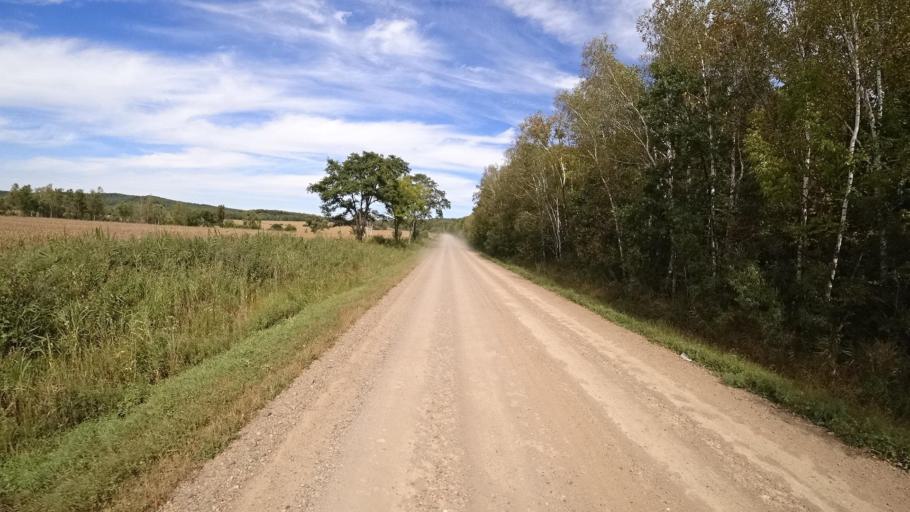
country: RU
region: Primorskiy
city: Yakovlevka
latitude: 44.5870
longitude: 133.6030
